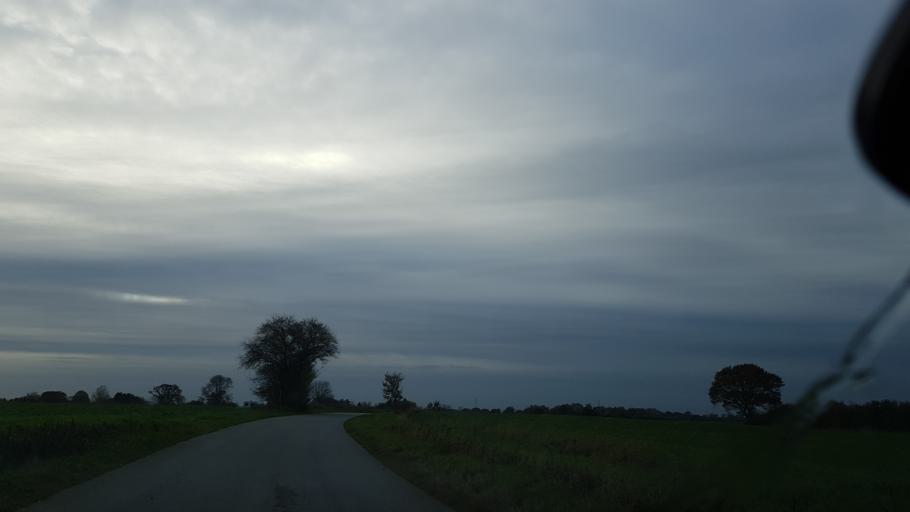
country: DK
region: South Denmark
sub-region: Haderslev Kommune
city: Vojens
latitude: 55.3046
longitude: 9.3861
